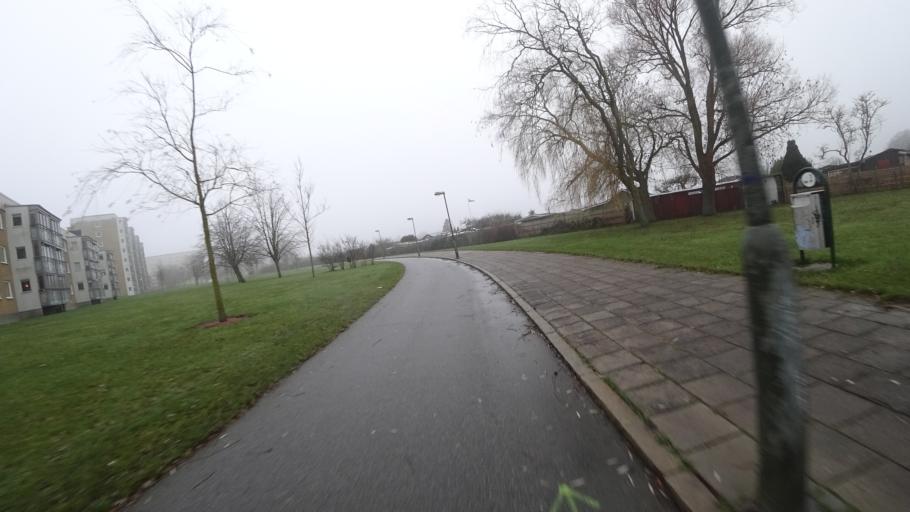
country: SE
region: Skane
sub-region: Malmo
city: Malmoe
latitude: 55.5780
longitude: 12.9890
